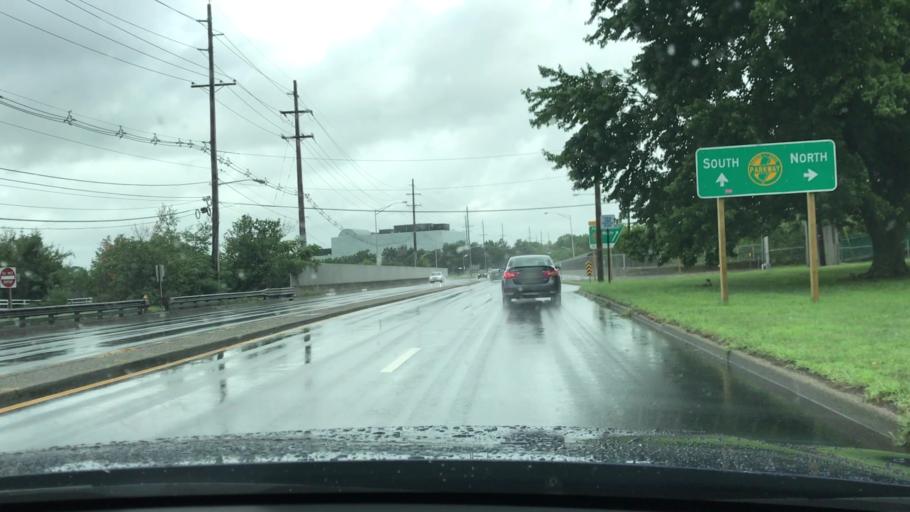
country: US
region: New Jersey
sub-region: Bergen County
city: Paramus
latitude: 40.9630
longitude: -74.0640
